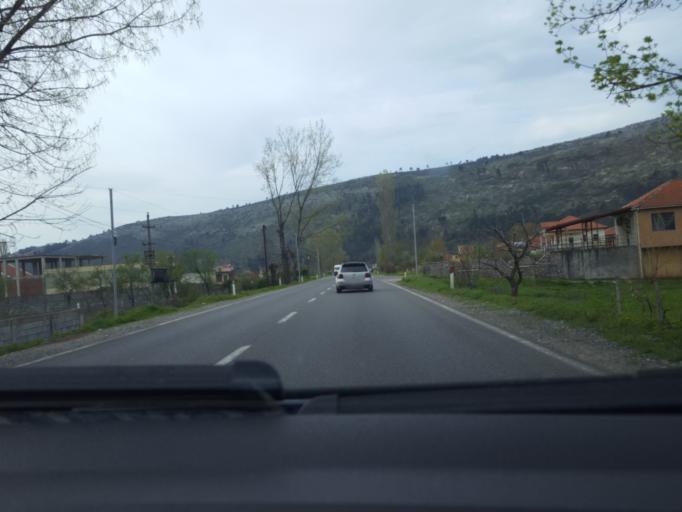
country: AL
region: Lezhe
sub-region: Rrethi i Lezhes
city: Balldreni i Ri
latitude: 41.8084
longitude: 19.6340
